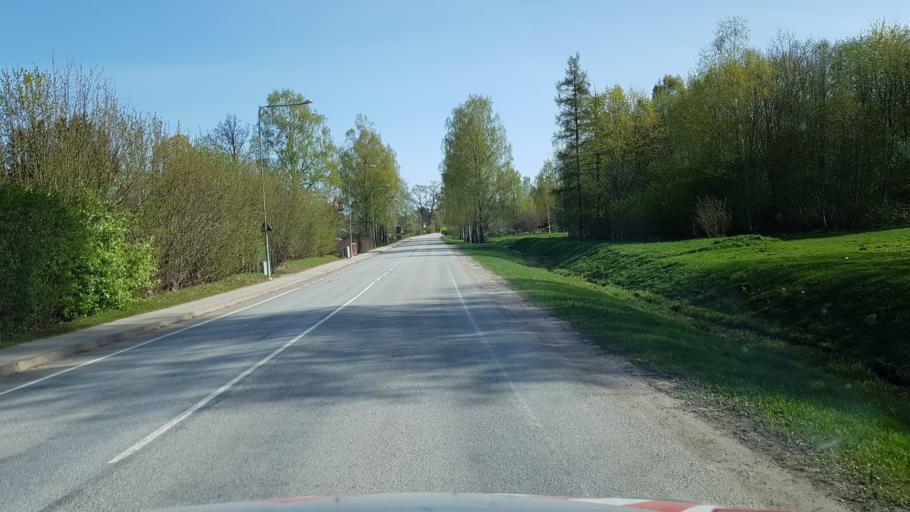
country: EE
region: Viljandimaa
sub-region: Abja vald
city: Abja-Paluoja
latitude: 58.1265
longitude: 25.3598
